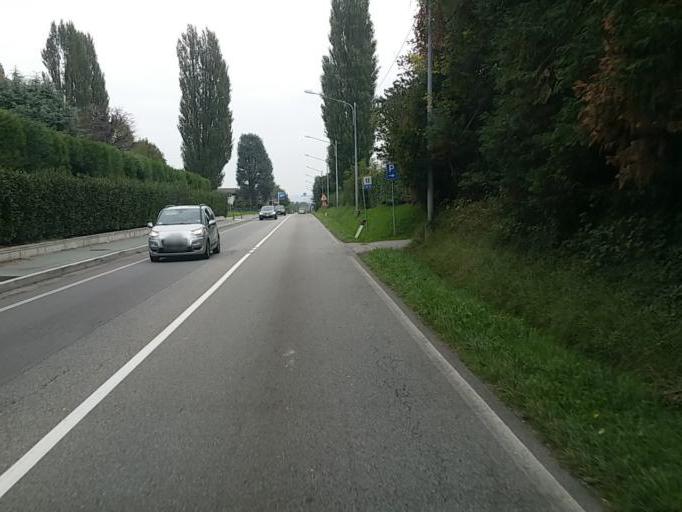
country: IT
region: Lombardy
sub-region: Provincia di Varese
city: Bodio
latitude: 45.7906
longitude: 8.7506
